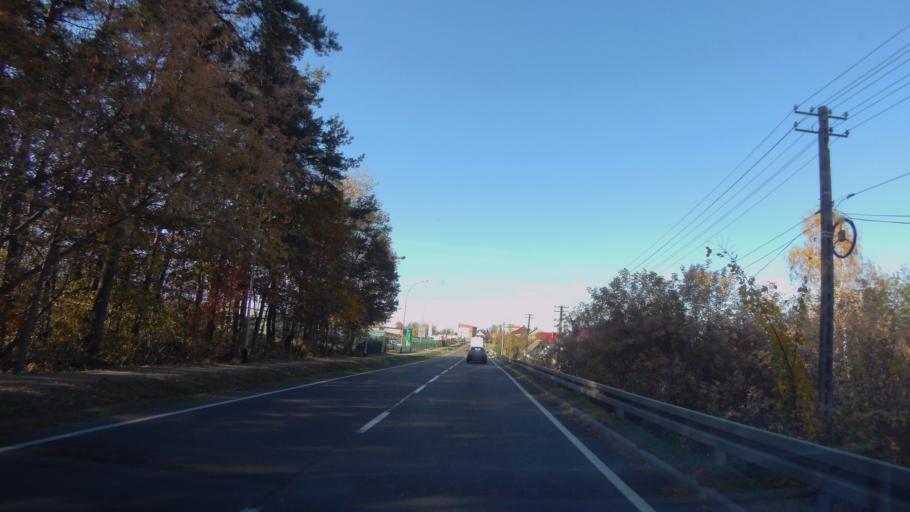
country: PL
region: Subcarpathian Voivodeship
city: Nowa Sarzyna
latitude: 50.3182
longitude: 22.3521
